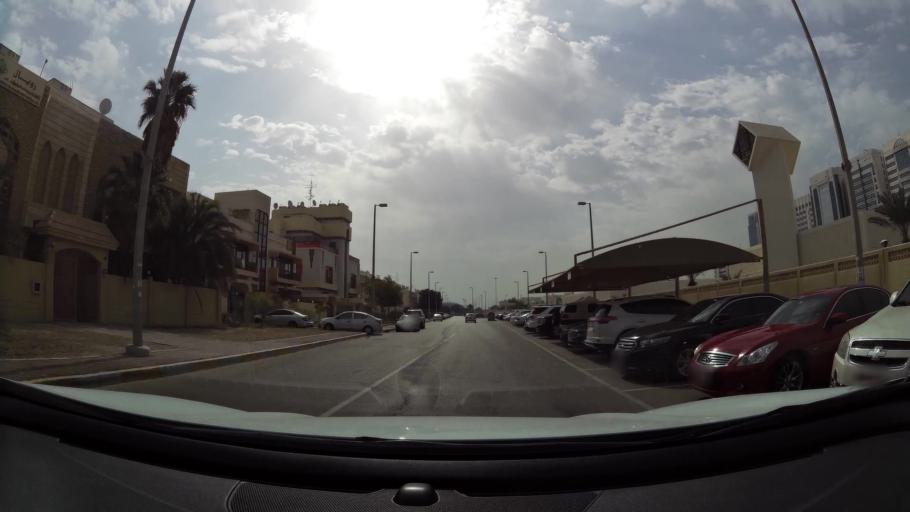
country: AE
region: Abu Dhabi
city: Abu Dhabi
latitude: 24.4617
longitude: 54.3819
